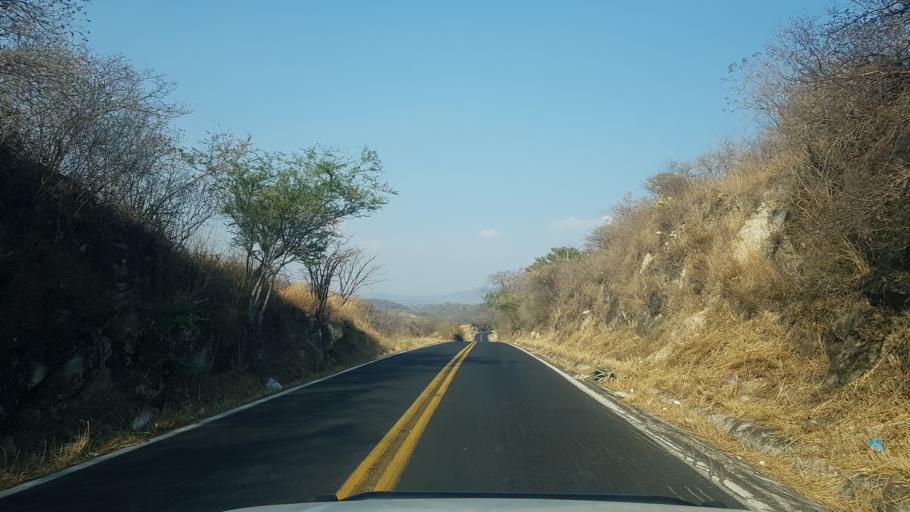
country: MX
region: Puebla
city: Calmeca
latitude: 18.6444
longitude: -98.6038
